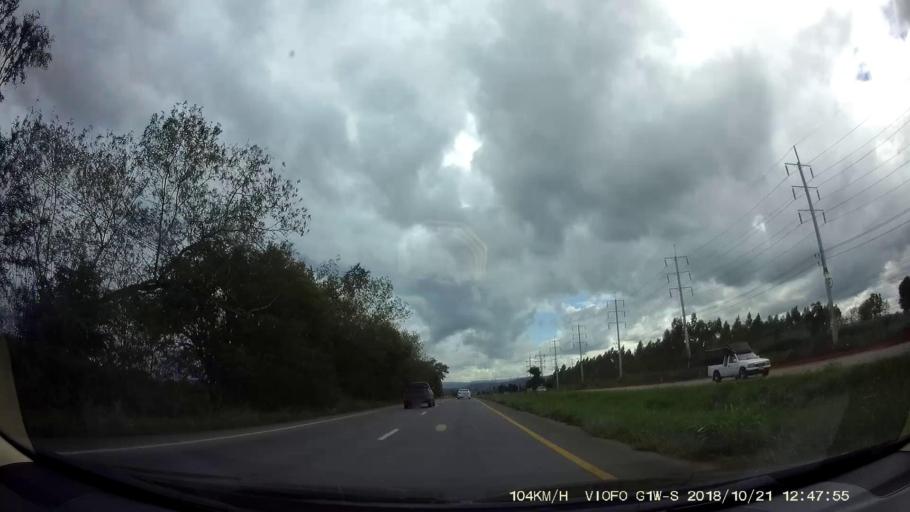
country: TH
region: Nakhon Ratchasima
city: Amphoe Sikhiu
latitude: 14.9211
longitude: 101.6840
